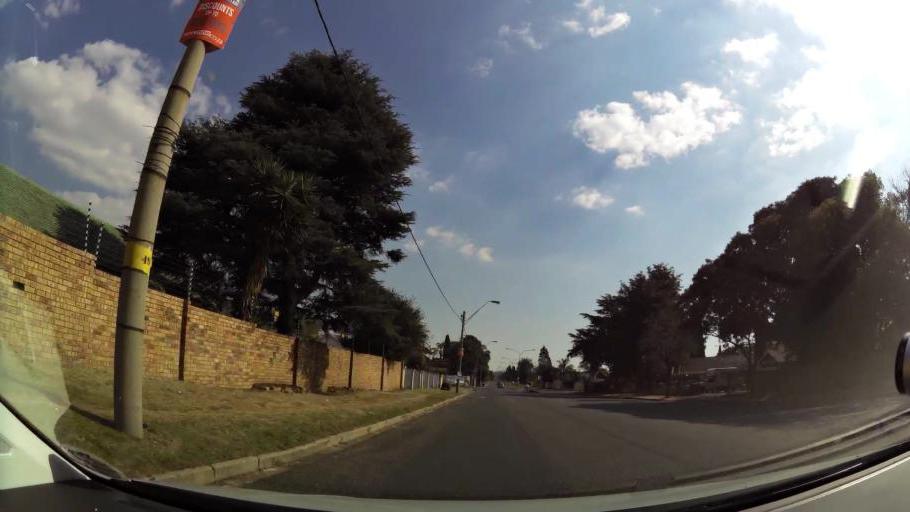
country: ZA
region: Gauteng
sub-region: City of Johannesburg Metropolitan Municipality
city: Modderfontein
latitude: -26.0908
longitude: 28.2380
